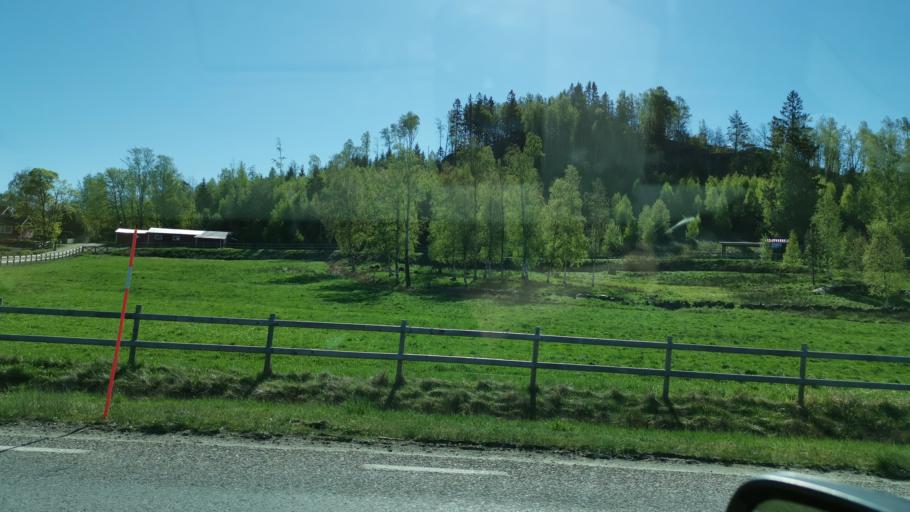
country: SE
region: Vaestra Goetaland
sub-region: Uddevalla Kommun
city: Ljungskile
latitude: 58.2793
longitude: 11.8884
